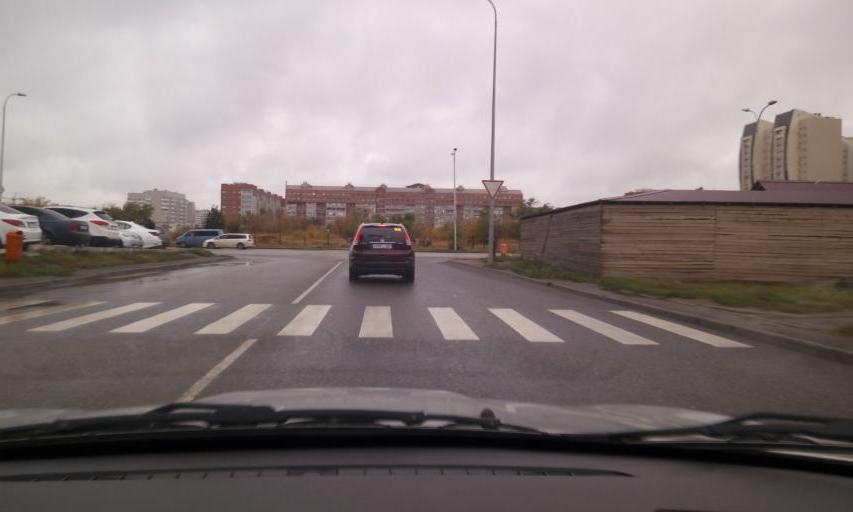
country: KZ
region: Astana Qalasy
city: Astana
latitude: 51.1617
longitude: 71.4028
